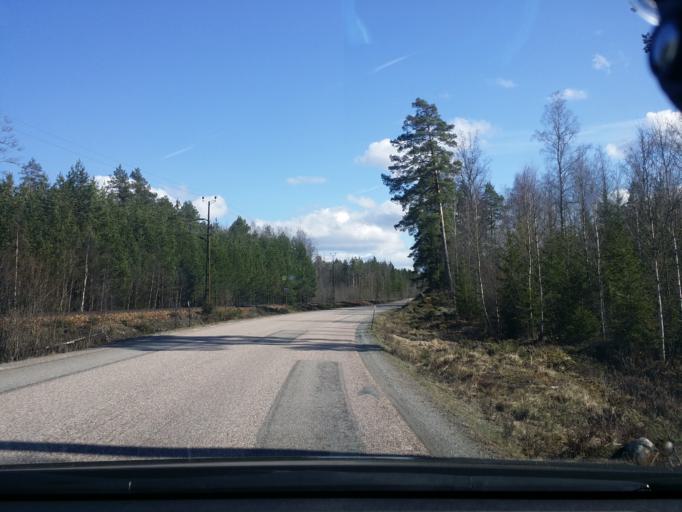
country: SE
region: Vaestmanland
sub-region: Sala Kommun
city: Sala
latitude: 59.9724
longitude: 16.5009
